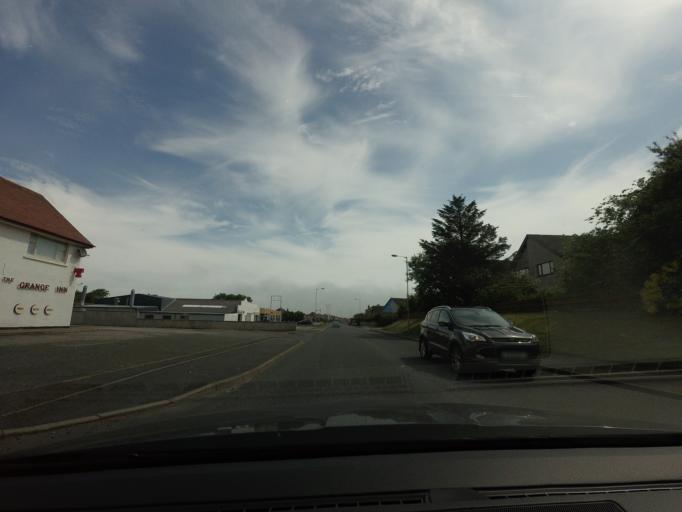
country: GB
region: Scotland
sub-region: Aberdeenshire
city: Peterhead
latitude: 57.5072
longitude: -1.8063
